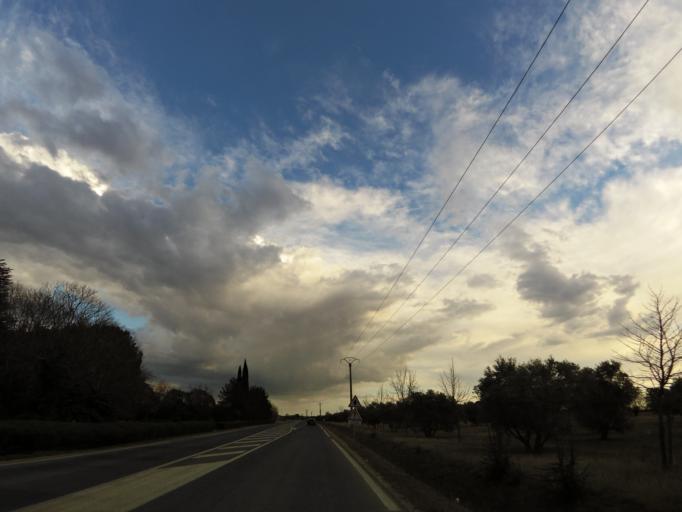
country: FR
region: Languedoc-Roussillon
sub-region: Departement du Gard
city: Codognan
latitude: 43.7295
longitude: 4.2394
